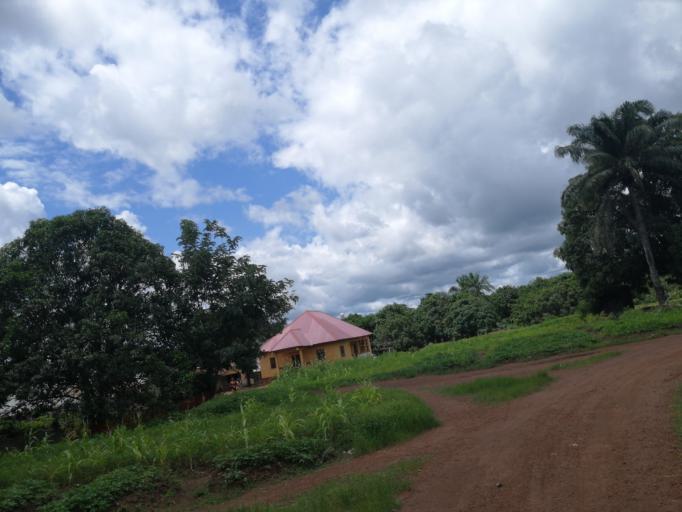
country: SL
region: Northern Province
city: Port Loko
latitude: 8.7703
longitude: -12.7804
